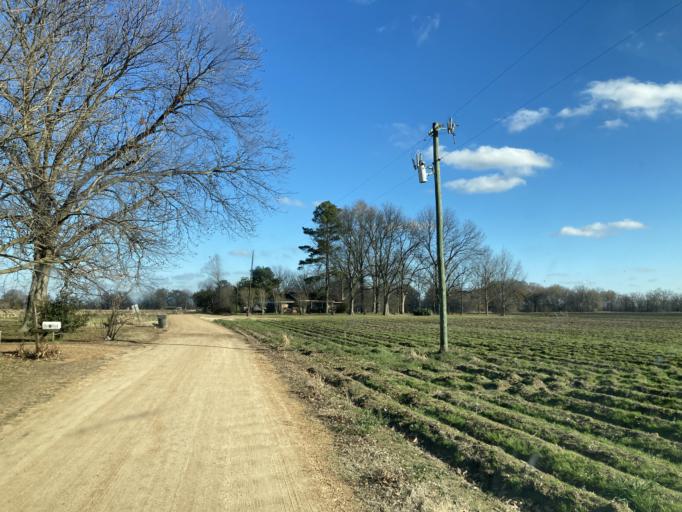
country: US
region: Mississippi
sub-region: Yazoo County
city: Yazoo City
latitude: 32.9316
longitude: -90.4719
